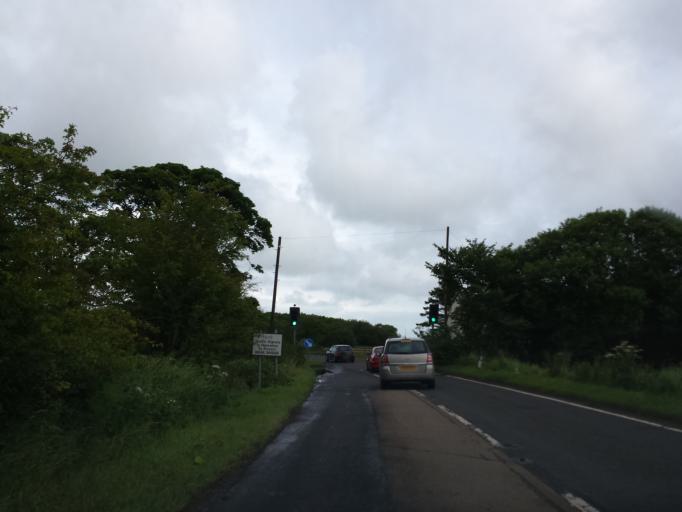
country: GB
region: Scotland
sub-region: Fife
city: Saint Andrews
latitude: 56.3060
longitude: -2.8253
